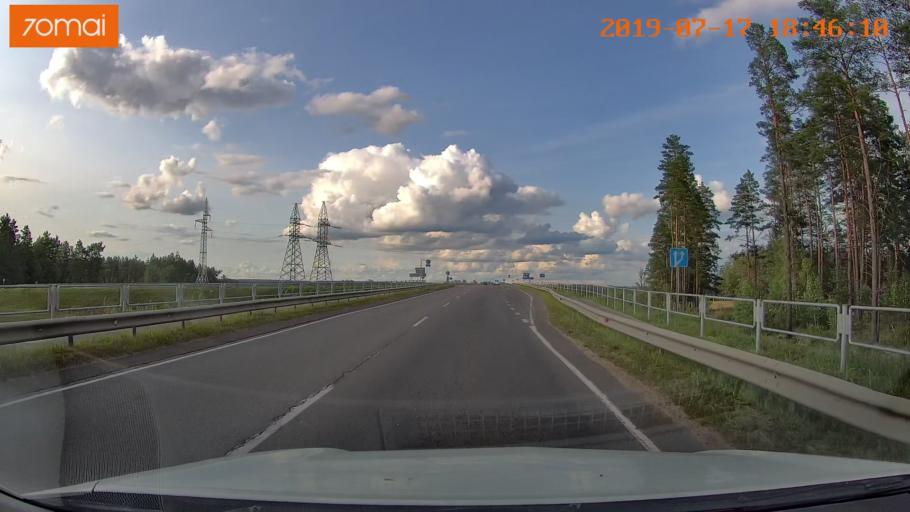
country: BY
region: Mogilev
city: Asipovichy
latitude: 53.3330
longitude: 28.6629
